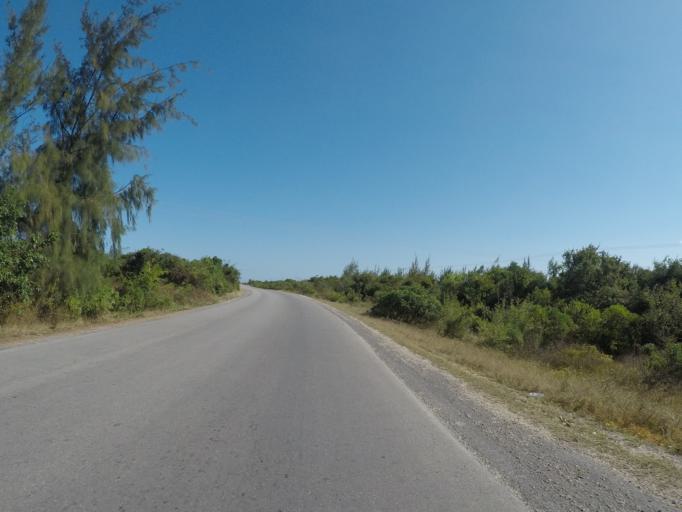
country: TZ
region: Zanzibar Central/South
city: Nganane
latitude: -6.2131
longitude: 39.5296
